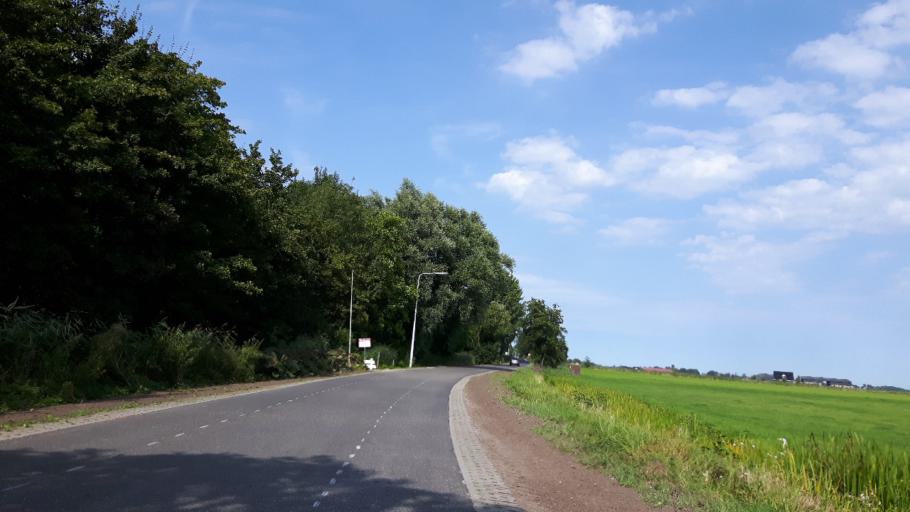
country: NL
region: Friesland
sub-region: Gemeente Ferwerderadiel
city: Burdaard
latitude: 53.2727
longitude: 5.8386
